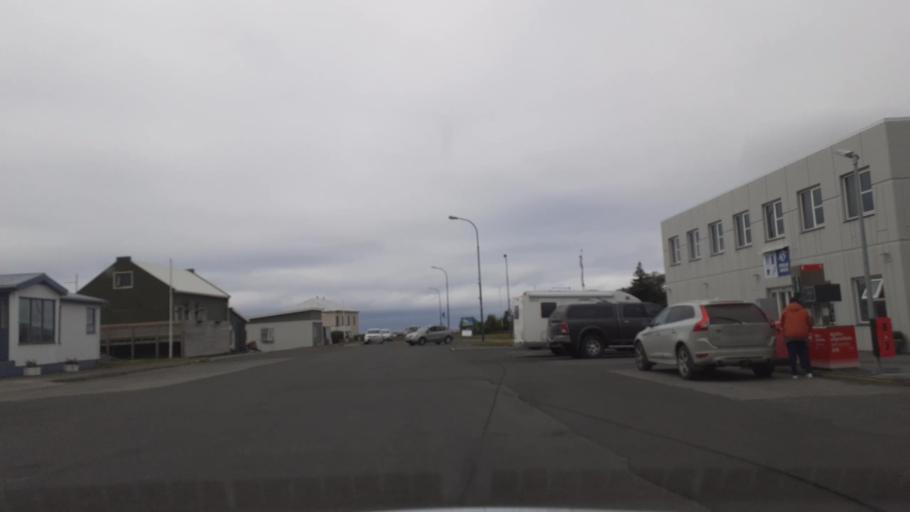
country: IS
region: Northwest
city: Saudarkrokur
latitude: 65.8969
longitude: -19.4126
